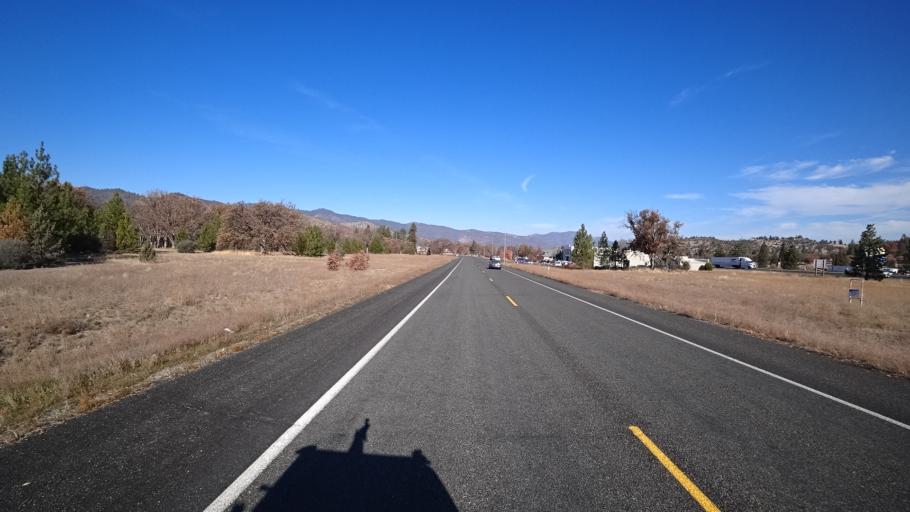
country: US
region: California
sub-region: Siskiyou County
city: Yreka
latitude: 41.6912
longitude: -122.6397
